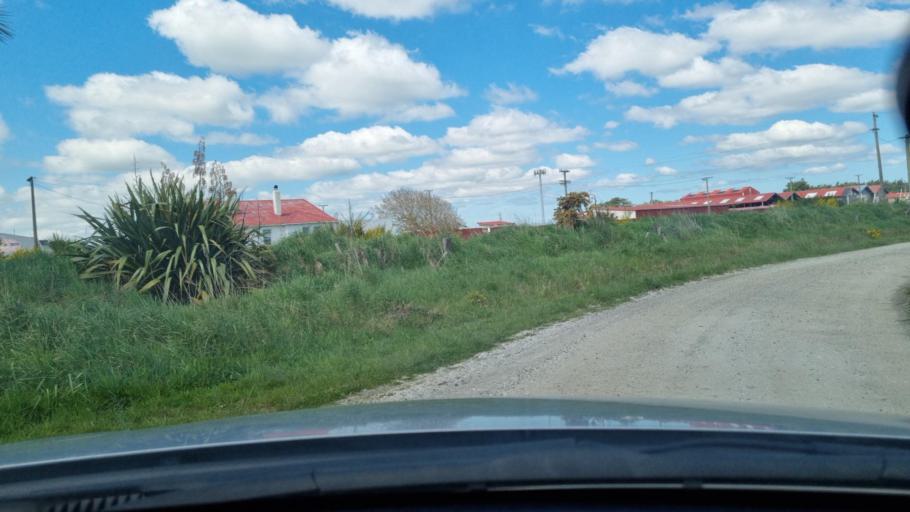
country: NZ
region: Southland
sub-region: Invercargill City
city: Invercargill
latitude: -46.3441
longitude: 168.3400
